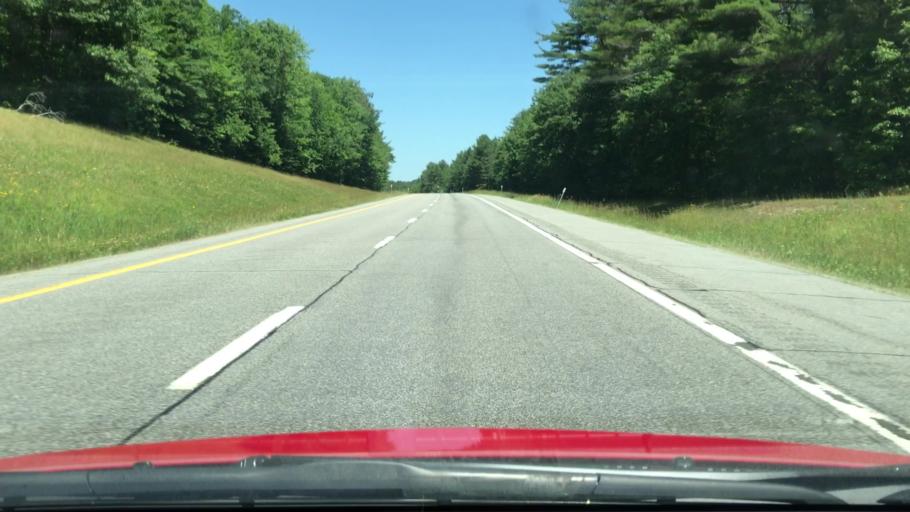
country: US
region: New York
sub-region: Essex County
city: Elizabethtown
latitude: 44.1516
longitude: -73.5827
